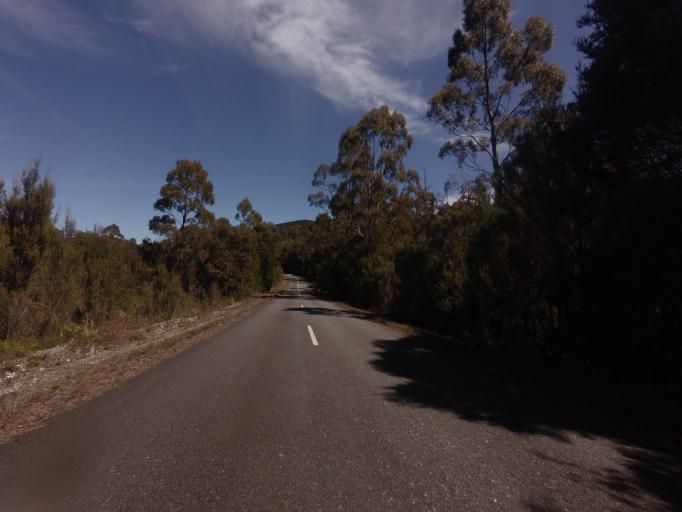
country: AU
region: Tasmania
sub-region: West Coast
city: Queenstown
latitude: -42.7747
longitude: 146.0397
